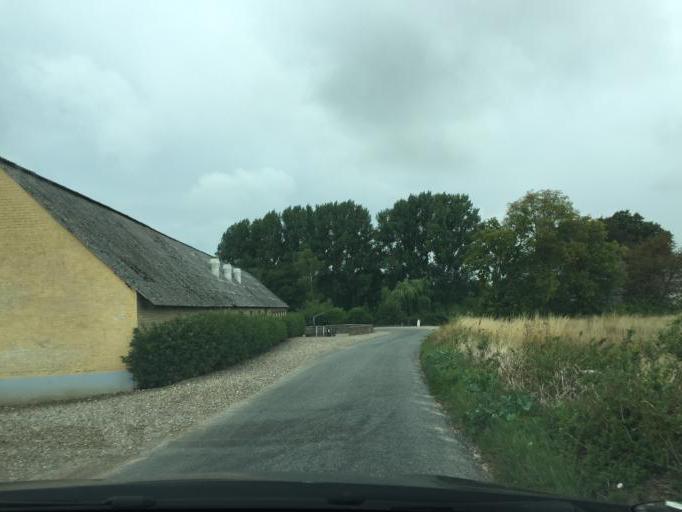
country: DK
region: South Denmark
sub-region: Assens Kommune
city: Harby
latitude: 55.1968
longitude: 10.0436
